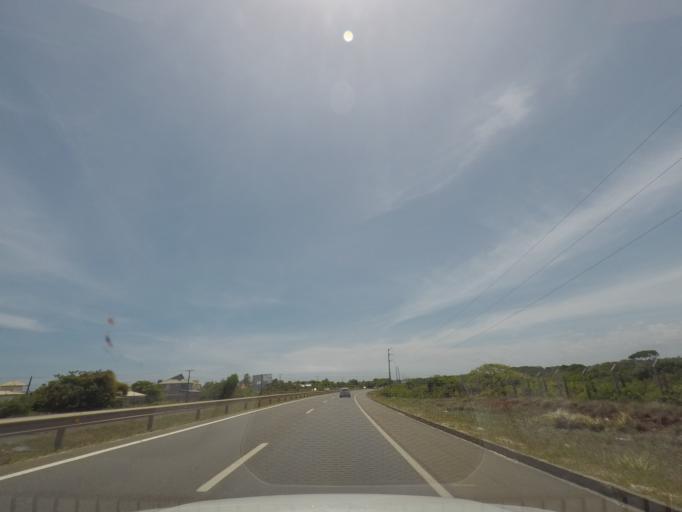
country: BR
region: Bahia
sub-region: Camacari
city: Camacari
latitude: -12.6818
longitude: -38.1068
